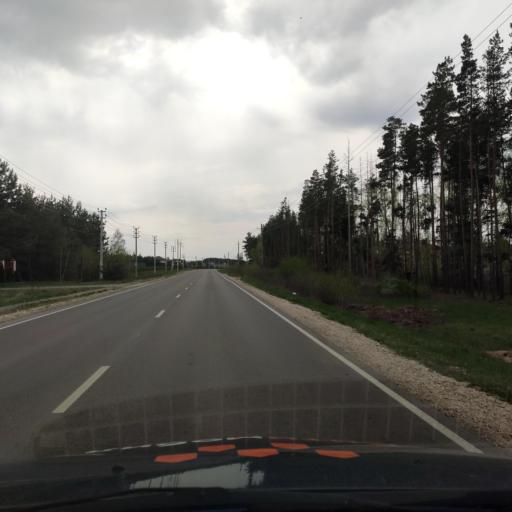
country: RU
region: Voronezj
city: Podgornoye
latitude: 51.8599
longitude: 39.1647
